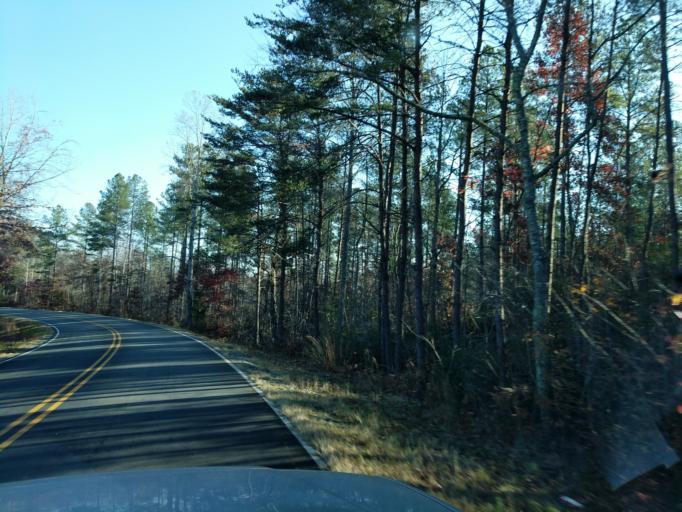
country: US
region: North Carolina
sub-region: Polk County
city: Columbus
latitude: 35.2630
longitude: -82.0618
